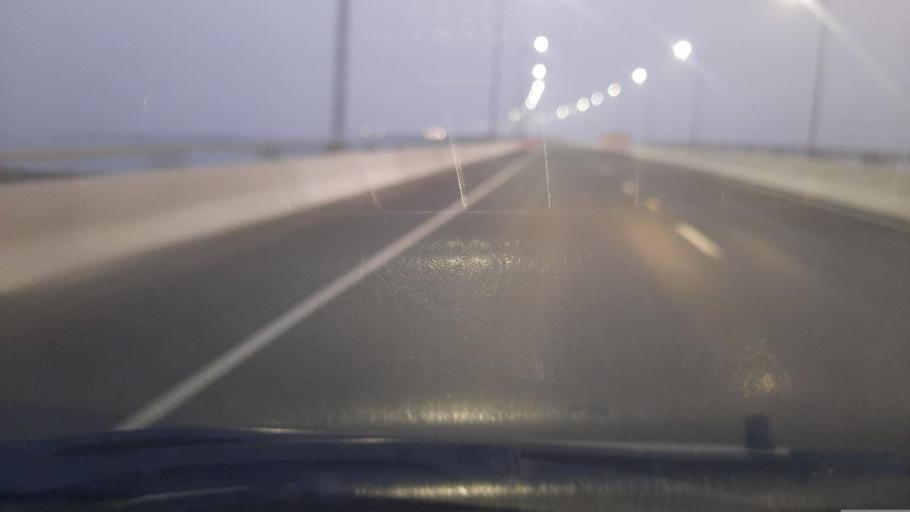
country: BD
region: Dhaka
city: Char Bhadrasan
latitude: 23.4141
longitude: 90.2584
